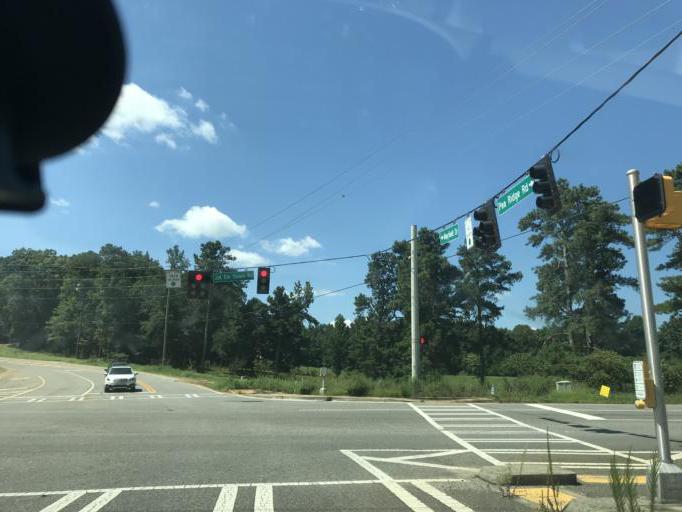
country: US
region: Georgia
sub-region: Dawson County
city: Dawsonville
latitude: 34.3082
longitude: -84.0289
